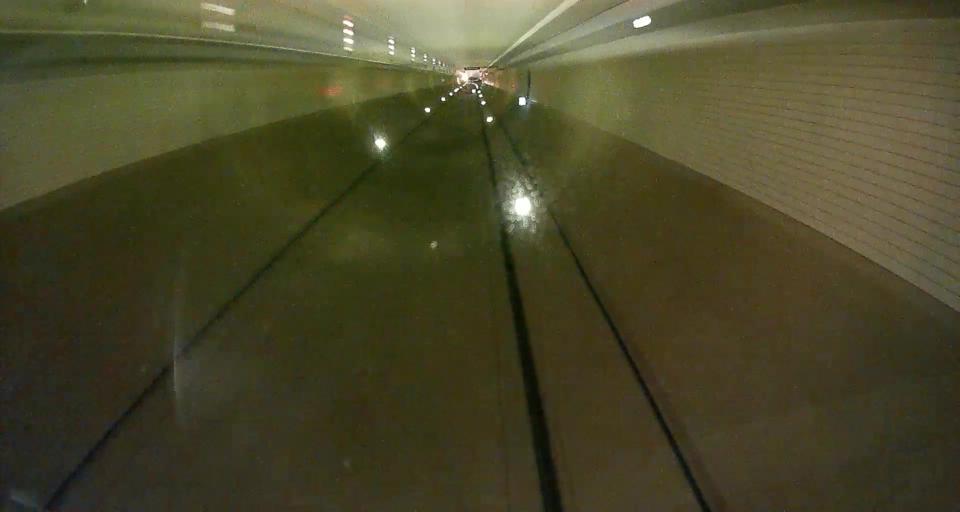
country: JP
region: Iwate
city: Miyako
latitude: 39.9311
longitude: 141.8580
